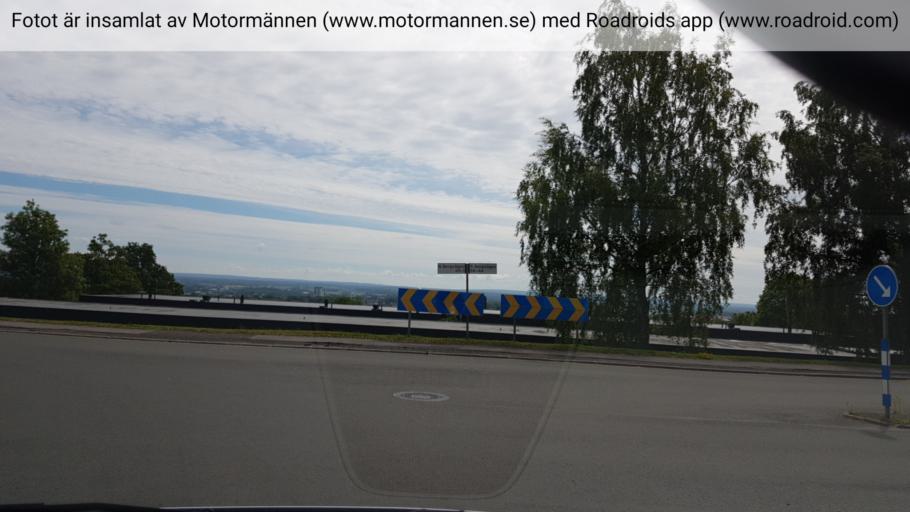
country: SE
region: Vaestra Goetaland
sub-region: Skovde Kommun
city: Skoevde
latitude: 58.3946
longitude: 13.8237
